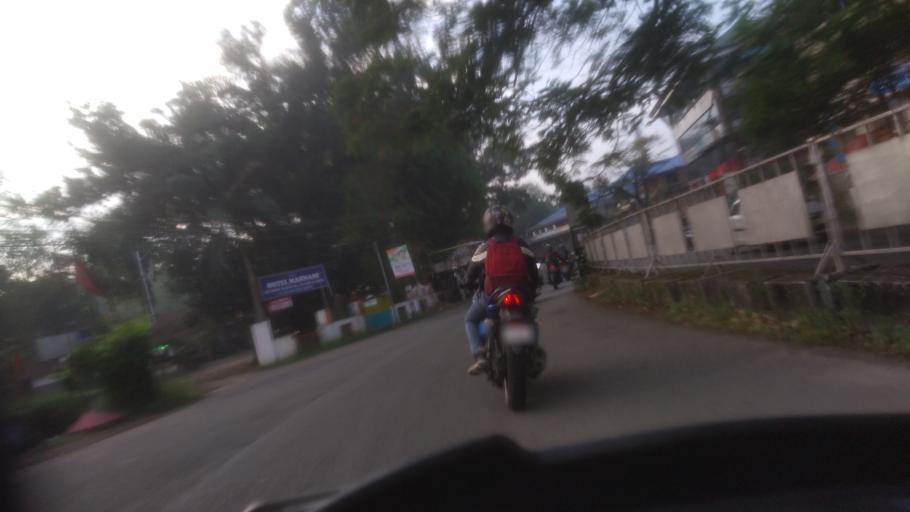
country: IN
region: Kerala
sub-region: Ernakulam
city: Aluva
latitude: 10.1104
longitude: 76.3591
